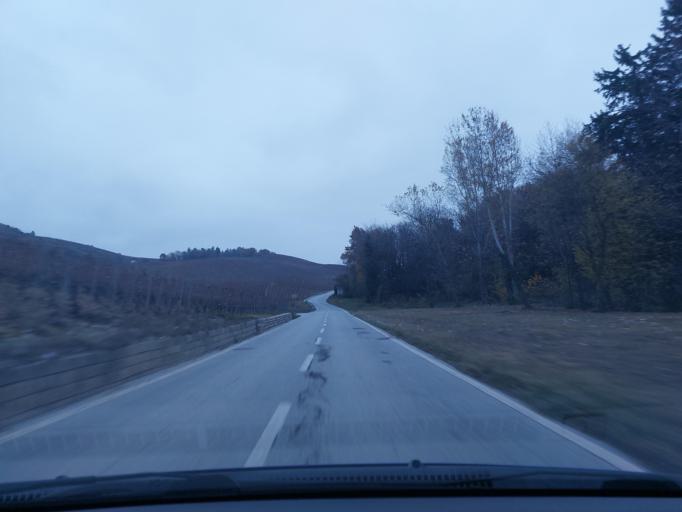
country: CH
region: Valais
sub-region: Sion District
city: Saviese
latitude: 46.2390
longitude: 7.3274
